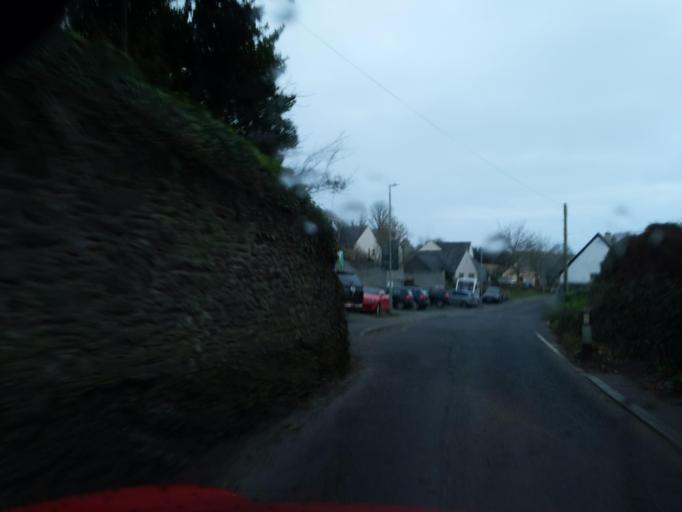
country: GB
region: England
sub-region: Devon
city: Wembury
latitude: 50.3287
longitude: -4.0667
